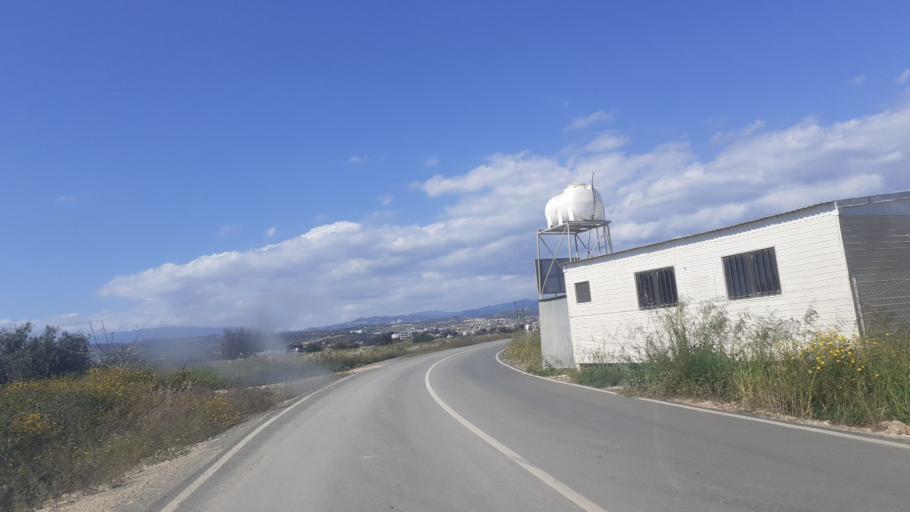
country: CY
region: Limassol
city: Ypsonas
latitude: 34.6720
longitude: 32.9865
